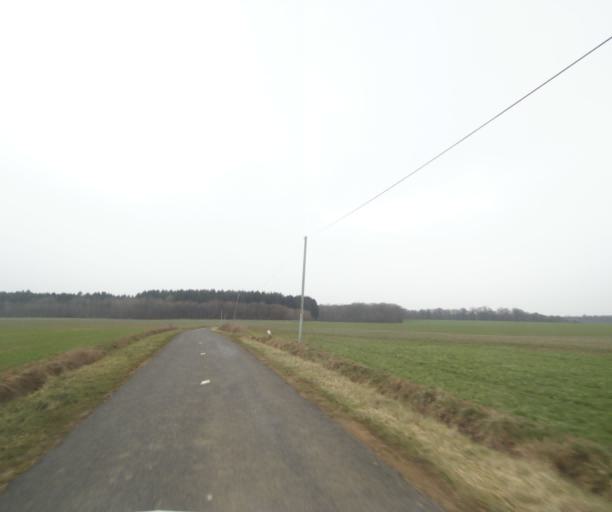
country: FR
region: Champagne-Ardenne
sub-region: Departement de la Haute-Marne
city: Chevillon
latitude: 48.4948
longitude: 5.0608
